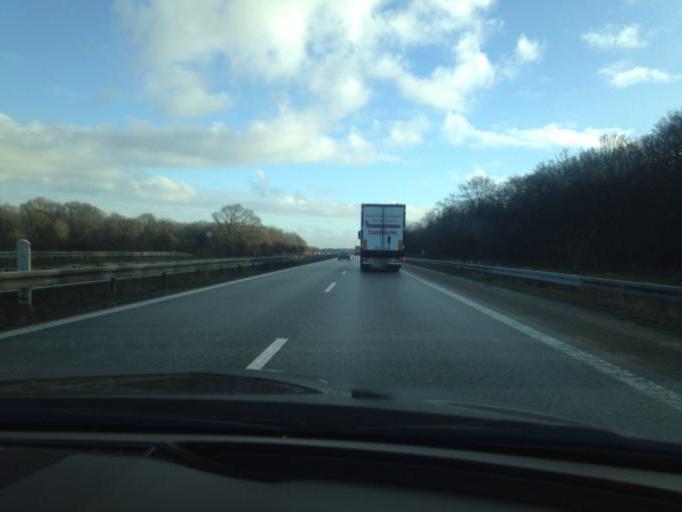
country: DK
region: South Denmark
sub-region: Vejen Kommune
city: Vejen
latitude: 55.4980
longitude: 9.0817
